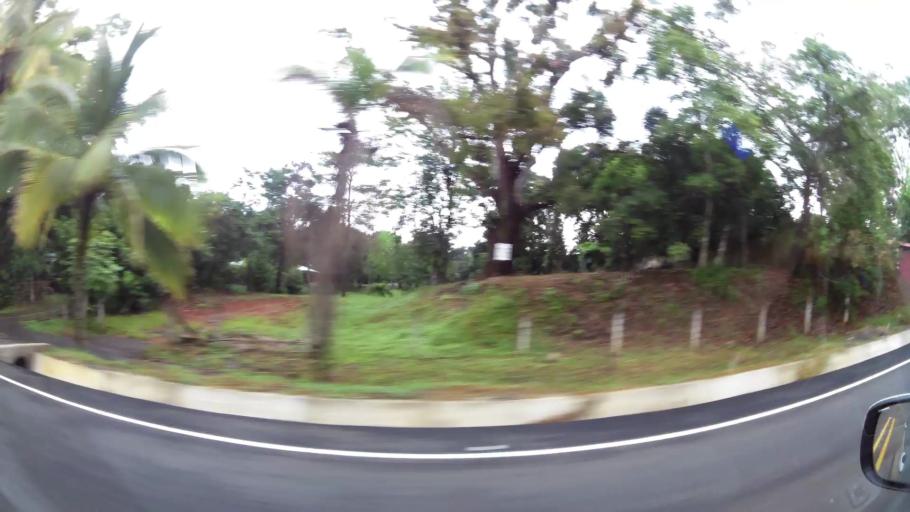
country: CR
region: Alajuela
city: Orotina
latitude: 9.9454
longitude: -84.5505
